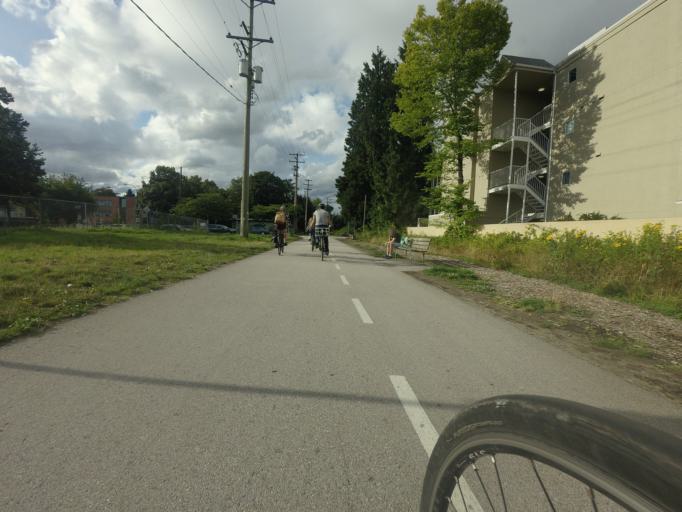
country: CA
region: British Columbia
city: West End
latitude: 49.2643
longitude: -123.1523
